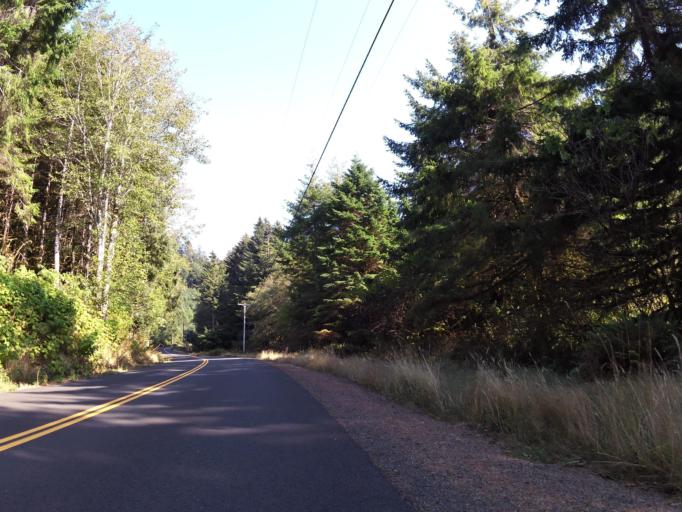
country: US
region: Oregon
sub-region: Lincoln County
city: Rose Lodge
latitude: 45.0834
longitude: -123.9493
